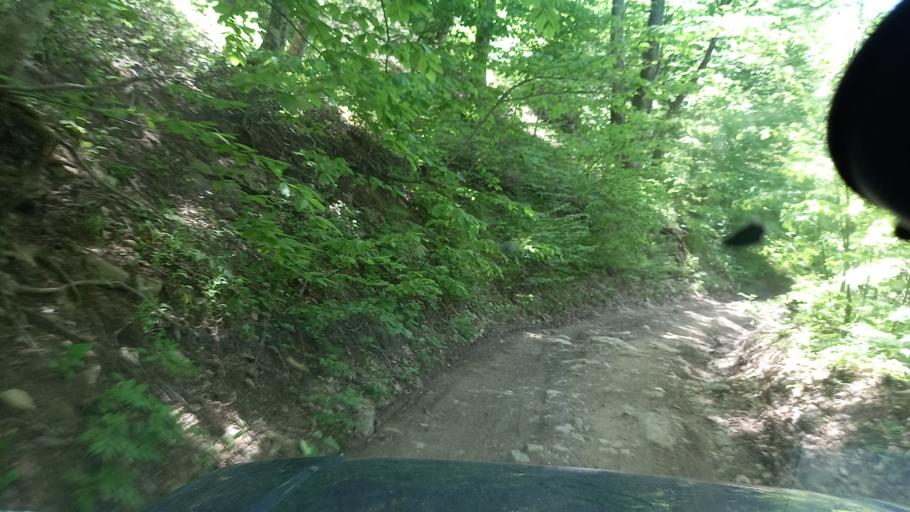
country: RU
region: Krasnodarskiy
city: Tuapse
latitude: 44.2504
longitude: 39.2836
